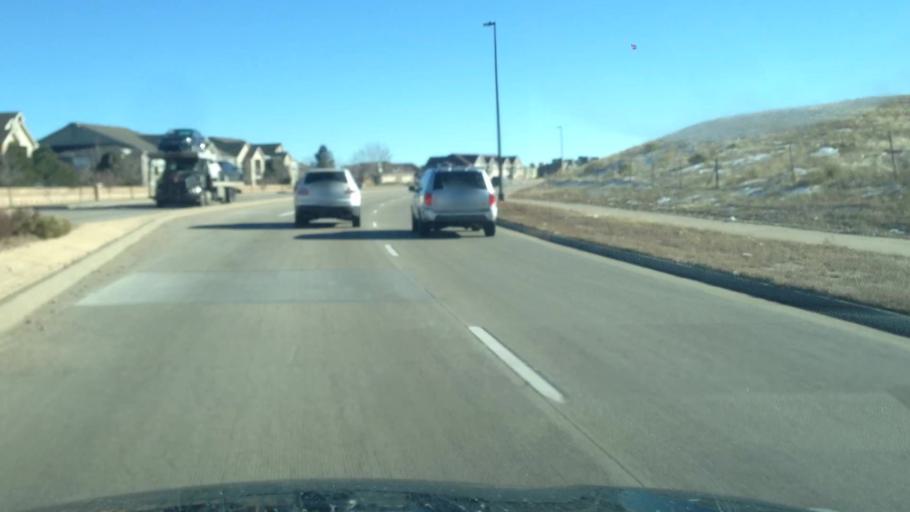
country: US
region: Colorado
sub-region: Arapahoe County
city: Dove Valley
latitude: 39.5805
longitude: -104.8094
